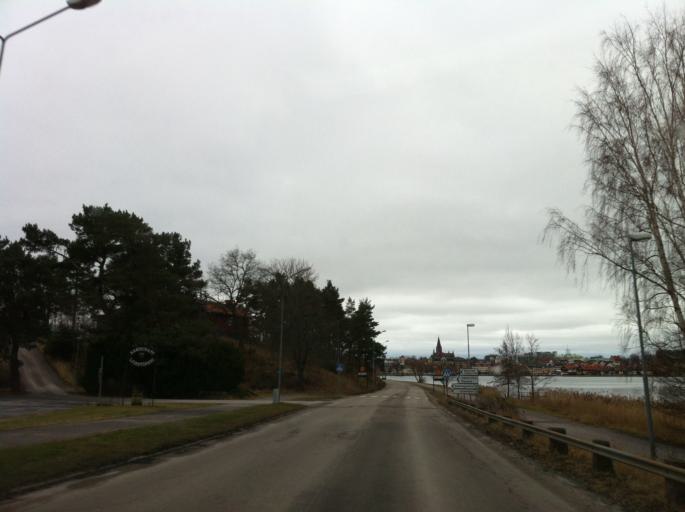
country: SE
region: Kalmar
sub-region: Vasterviks Kommun
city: Vaestervik
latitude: 57.8031
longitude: 16.6062
